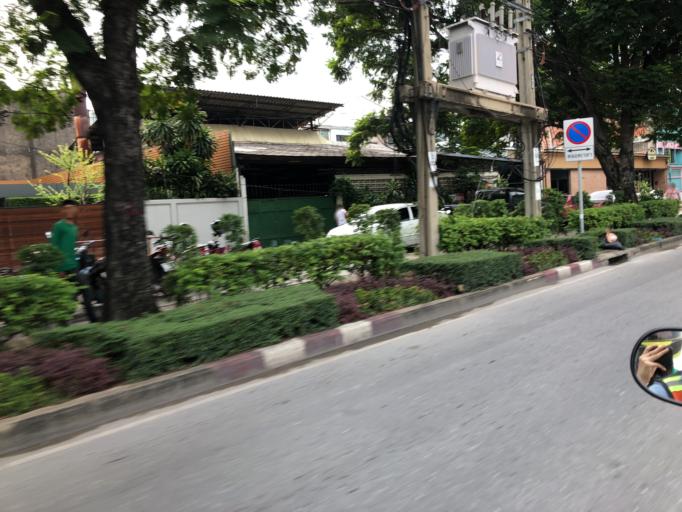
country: TH
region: Bangkok
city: Yan Nawa
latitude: 13.7056
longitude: 100.5387
